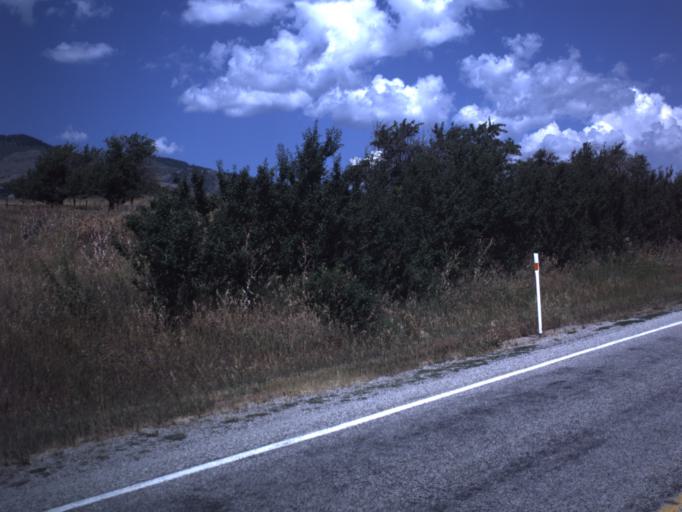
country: US
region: Idaho
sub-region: Bear Lake County
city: Paris
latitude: 41.9933
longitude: -111.4112
